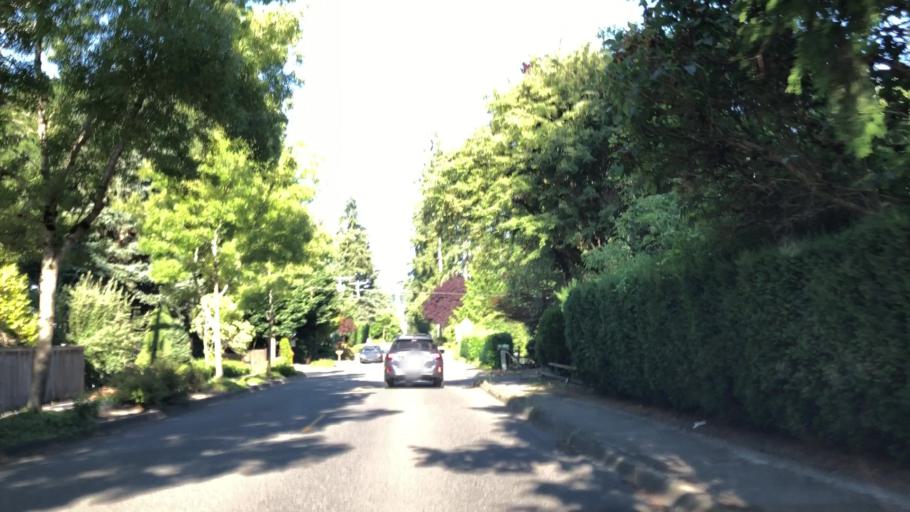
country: US
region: Washington
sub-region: King County
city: Medina
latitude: 47.6320
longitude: -122.2383
